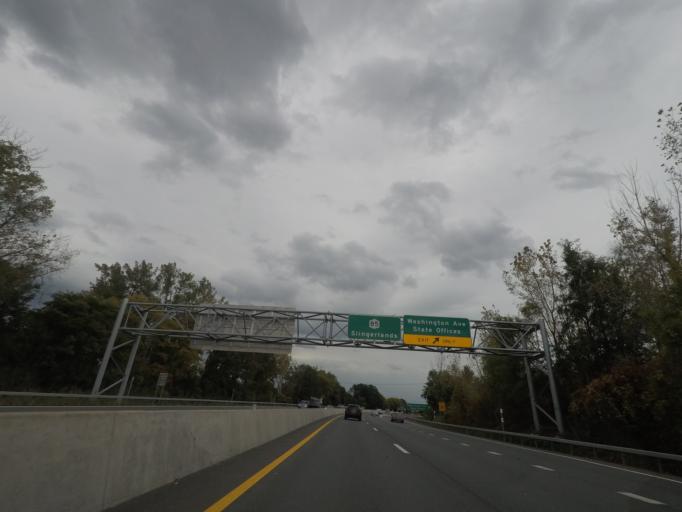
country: US
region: New York
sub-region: Albany County
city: Roessleville
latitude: 42.6839
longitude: -73.8020
